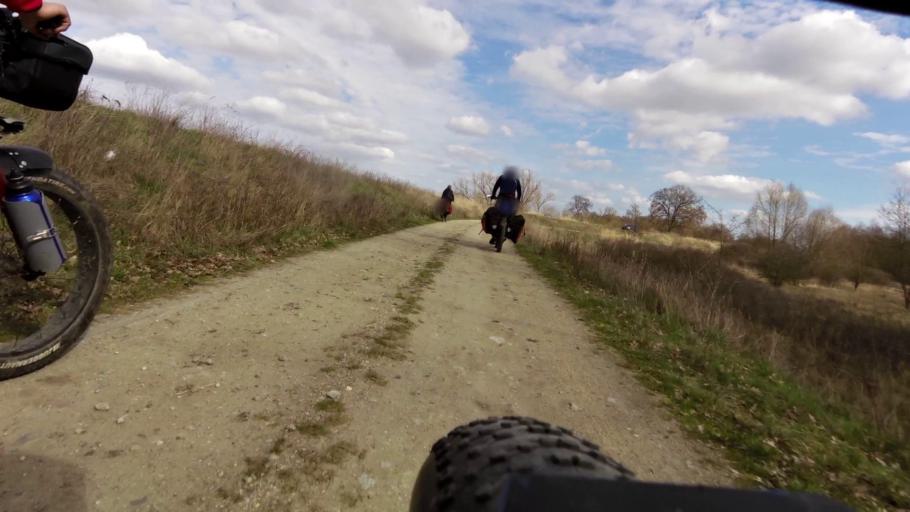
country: DE
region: Brandenburg
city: Lebus
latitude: 52.4379
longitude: 14.5641
